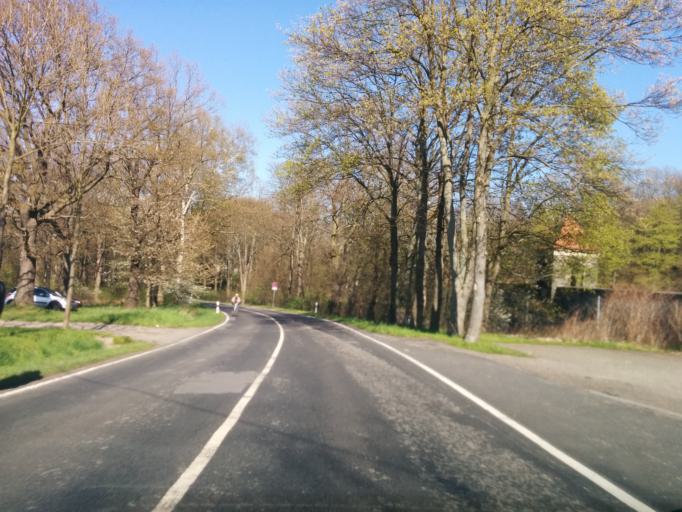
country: DE
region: Saxony
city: Niederwiesa
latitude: 50.8332
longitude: 13.0096
